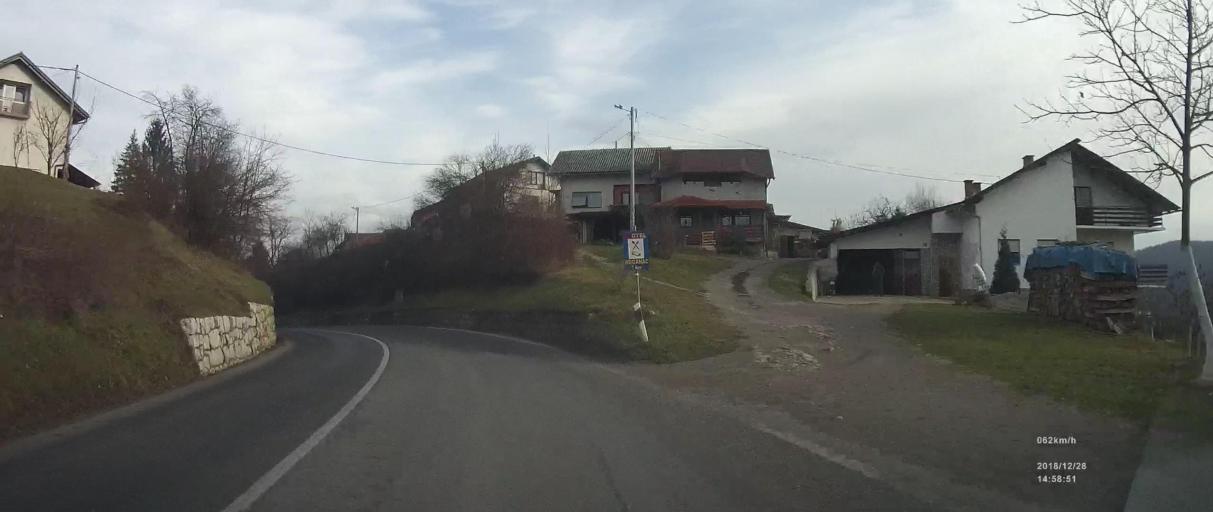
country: HR
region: Karlovacka
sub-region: Grad Karlovac
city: Karlovac
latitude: 45.4572
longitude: 15.4748
